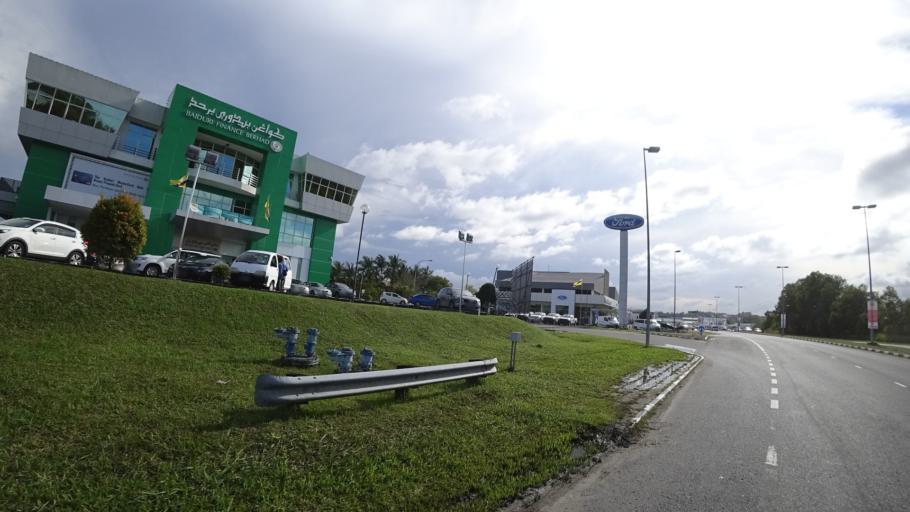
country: BN
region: Brunei and Muara
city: Bandar Seri Begawan
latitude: 4.8958
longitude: 114.9082
